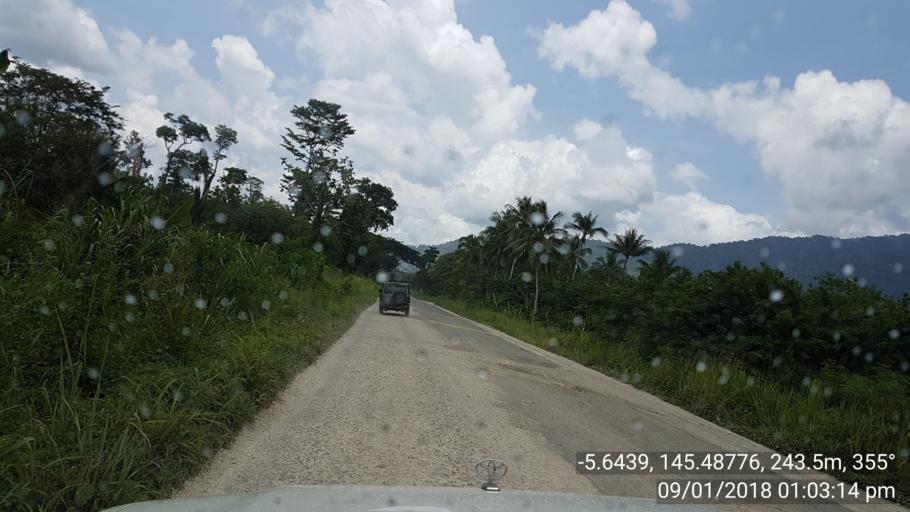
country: PG
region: Eastern Highlands
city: Goroka
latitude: -5.6438
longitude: 145.4878
